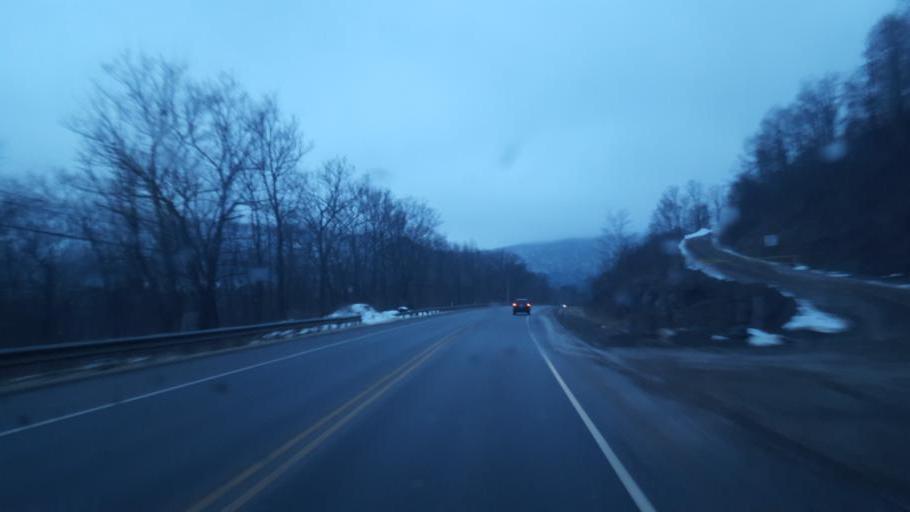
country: US
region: Pennsylvania
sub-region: McKean County
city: Port Allegany
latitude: 41.7911
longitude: -78.2304
